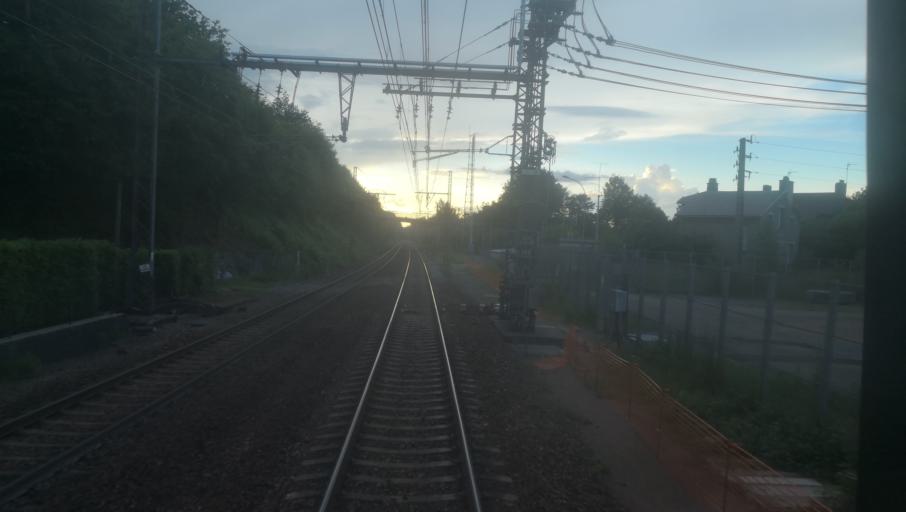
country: FR
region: Limousin
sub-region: Departement de la Creuse
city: La Souterraine
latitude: 46.2467
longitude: 1.4862
